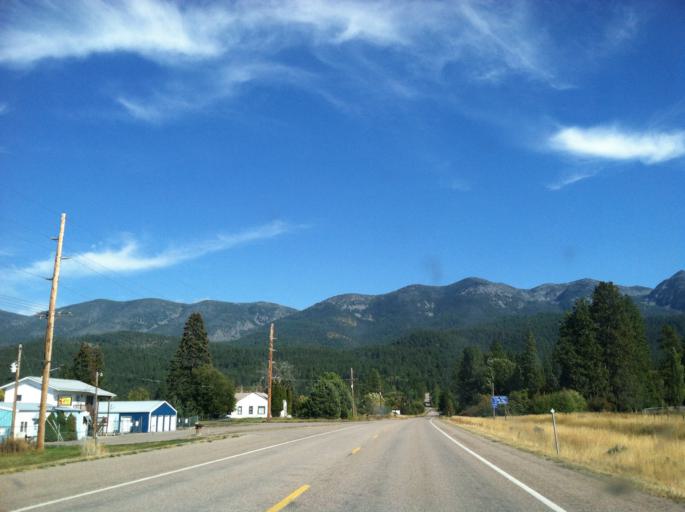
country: US
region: Montana
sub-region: Lake County
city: Polson
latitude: 47.6888
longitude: -114.0686
